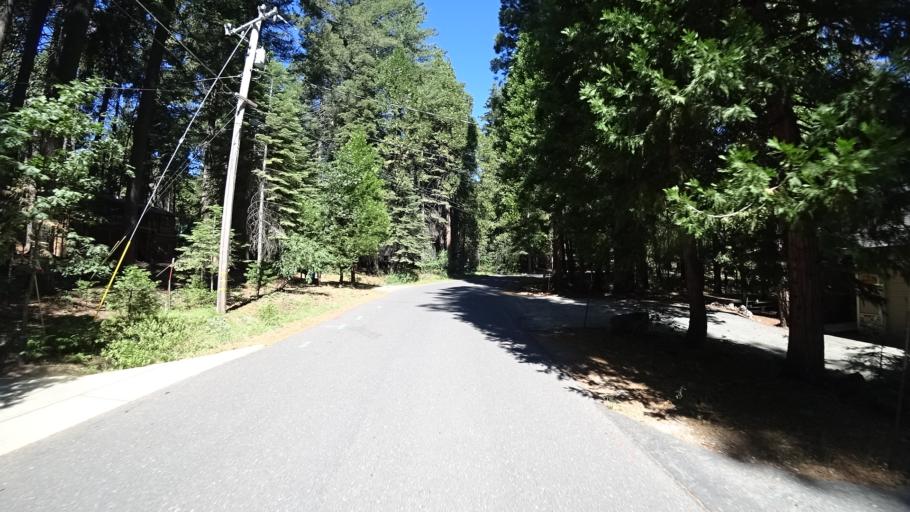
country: US
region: California
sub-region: Calaveras County
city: Arnold
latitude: 38.2901
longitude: -120.2815
